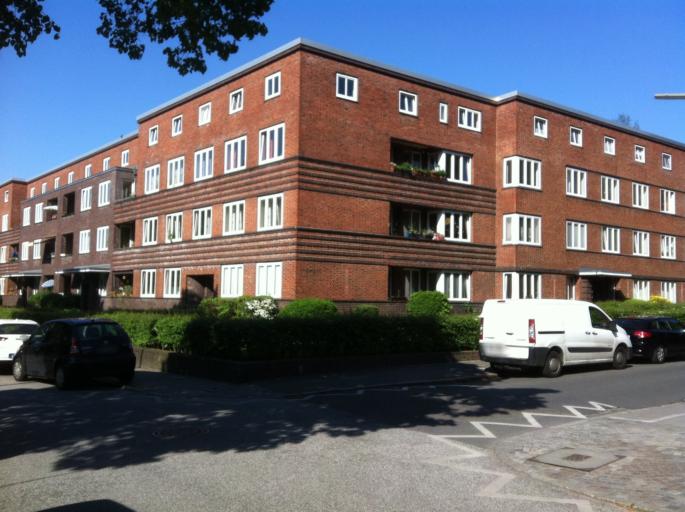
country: DE
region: Hamburg
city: Altona
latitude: 53.5535
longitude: 9.9095
